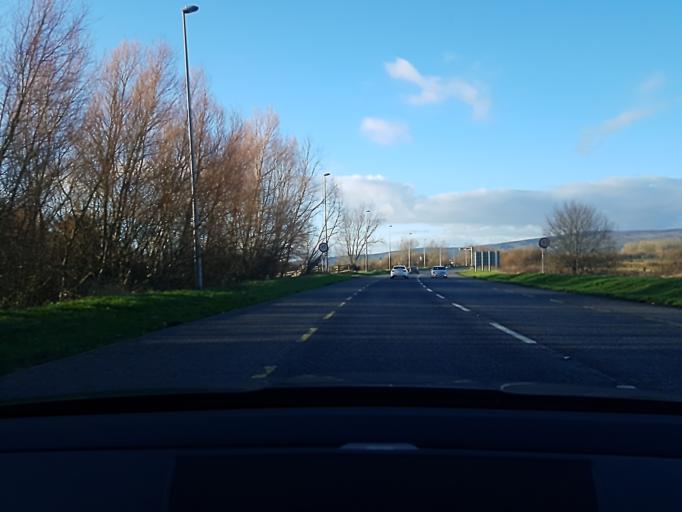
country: IE
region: Munster
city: Moyross
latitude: 52.6663
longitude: -8.6715
